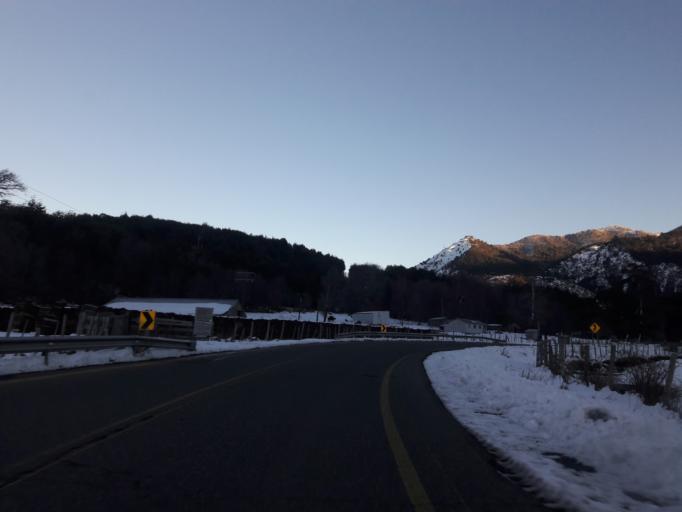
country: CL
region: Araucania
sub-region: Provincia de Cautin
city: Vilcun
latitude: -38.5001
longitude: -71.5194
